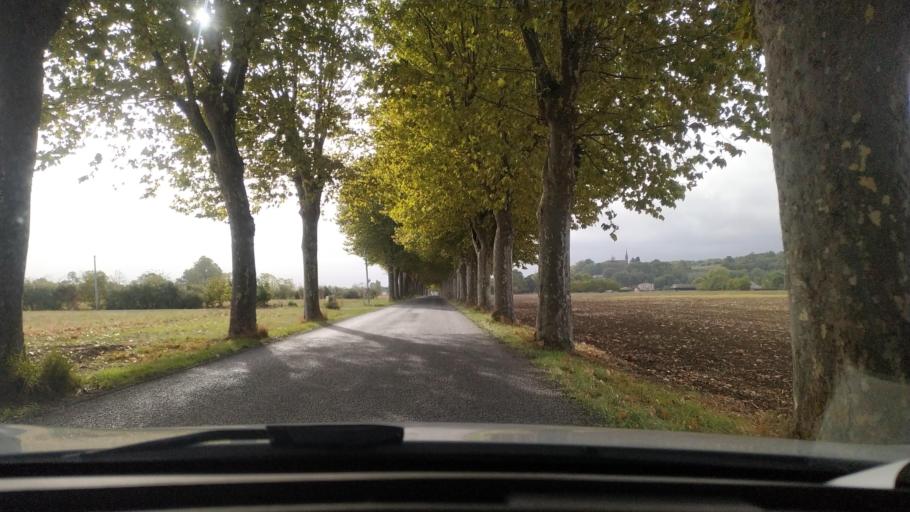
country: FR
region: Midi-Pyrenees
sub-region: Departement de la Haute-Garonne
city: Gaillac-Toulza
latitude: 43.2812
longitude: 1.4951
